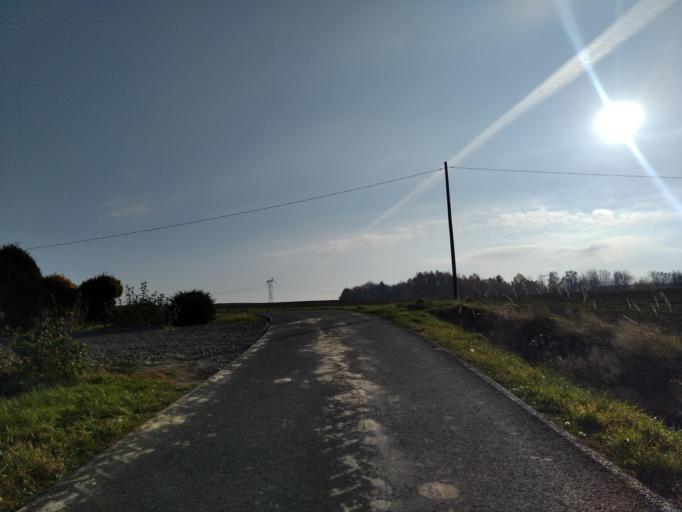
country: PL
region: Subcarpathian Voivodeship
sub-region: Powiat strzyzowski
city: Babica
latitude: 49.9021
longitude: 21.8439
